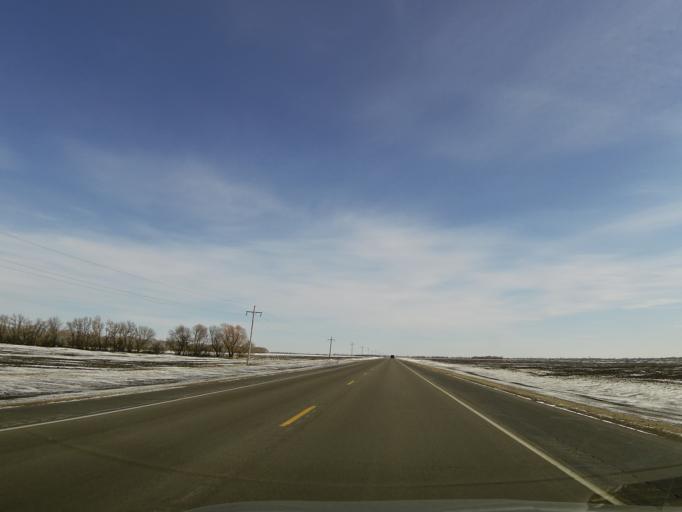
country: US
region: North Dakota
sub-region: Walsh County
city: Grafton
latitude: 48.4123
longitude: -97.3131
